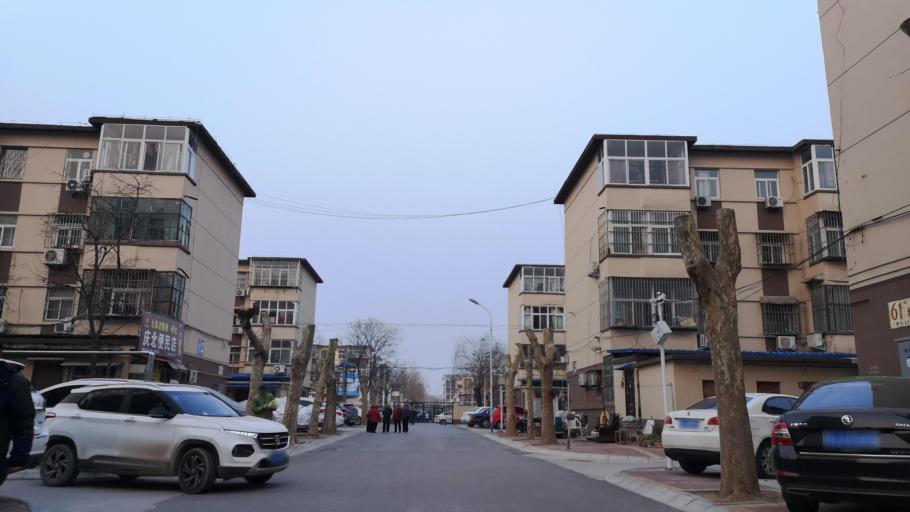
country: CN
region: Henan Sheng
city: Zhongyuanlu
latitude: 35.7839
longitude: 115.0731
